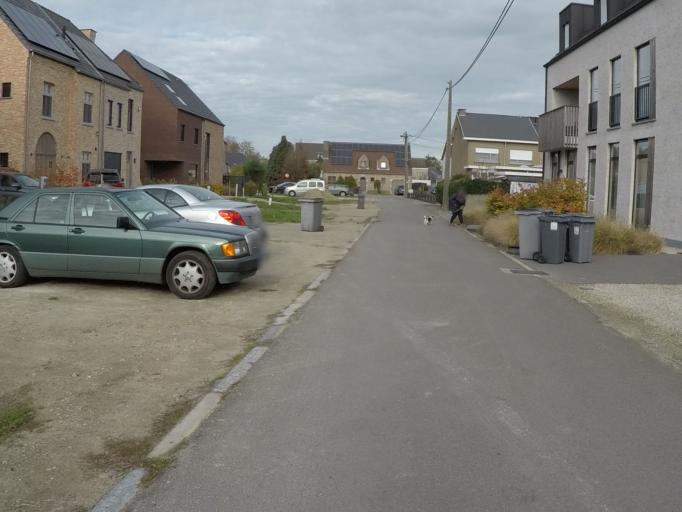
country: BE
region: Flanders
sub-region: Provincie Antwerpen
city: Berlaar
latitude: 51.1418
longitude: 4.6352
